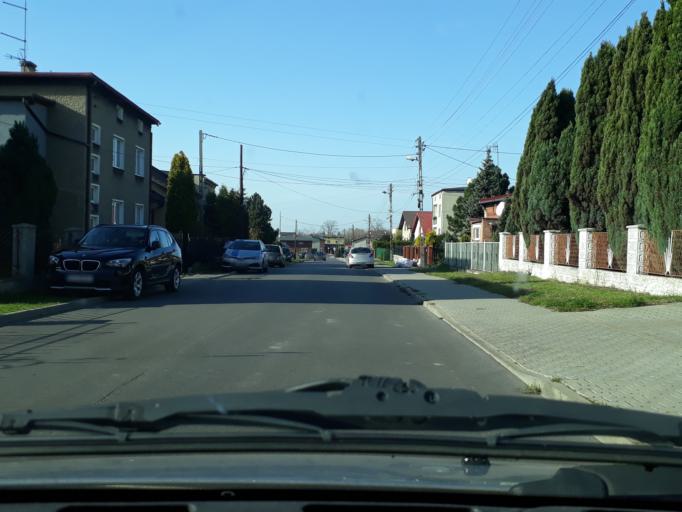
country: PL
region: Silesian Voivodeship
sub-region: Powiat tarnogorski
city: Tarnowskie Gory
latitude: 50.4220
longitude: 18.8802
